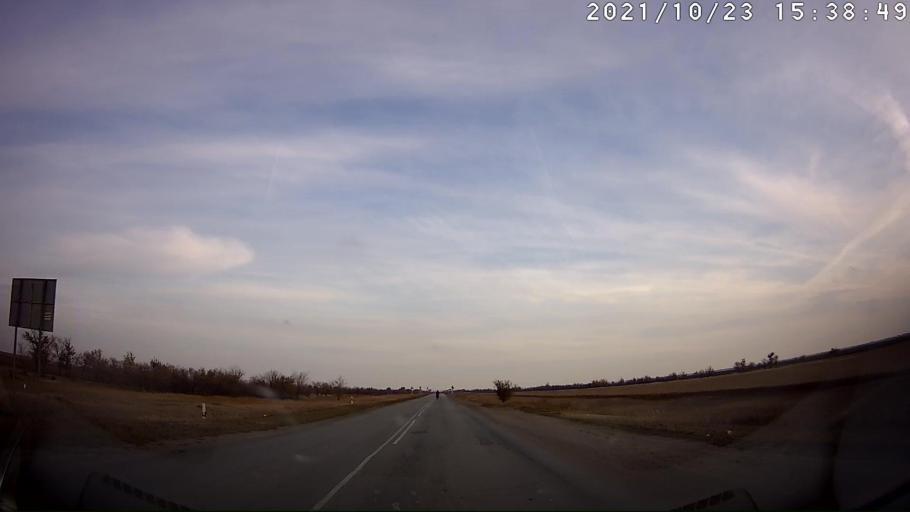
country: RU
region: Volgograd
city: Bereslavka
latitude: 48.1302
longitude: 44.1199
